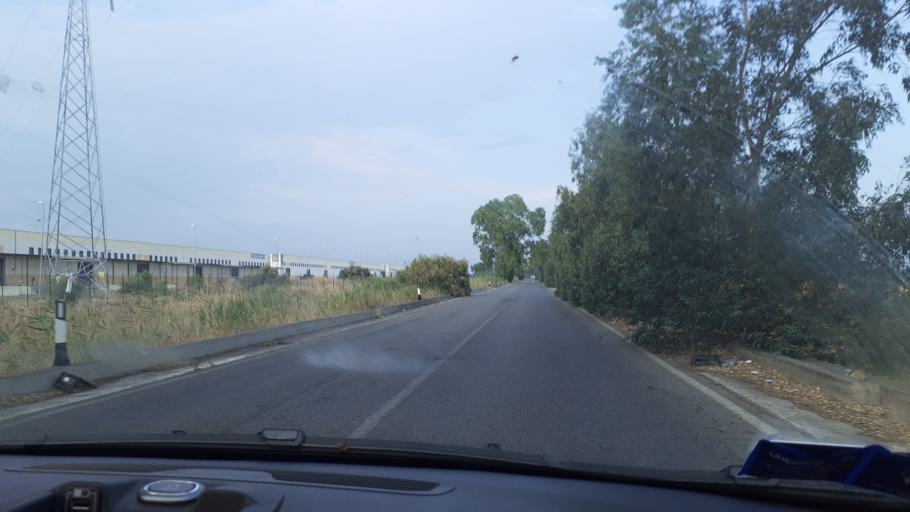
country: IT
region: Sicily
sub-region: Catania
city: Misterbianco
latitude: 37.4436
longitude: 15.0136
